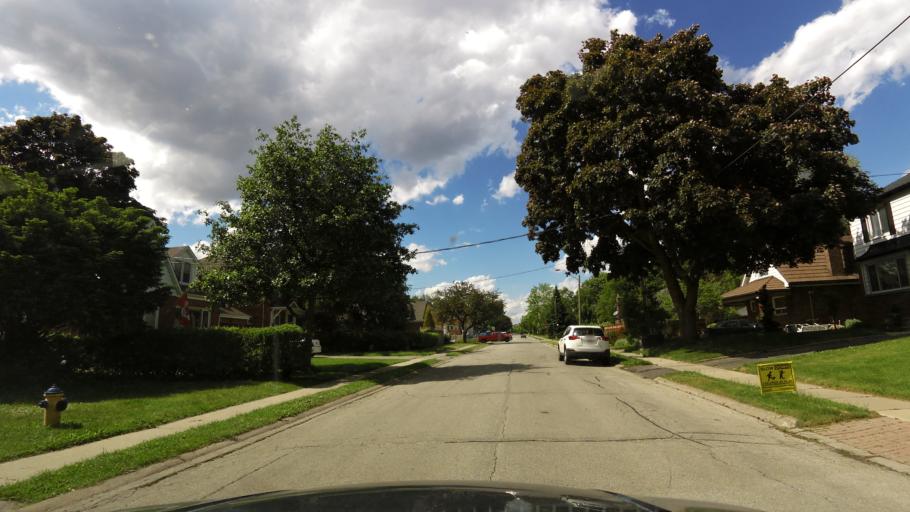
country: CA
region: Ontario
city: Etobicoke
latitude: 43.5904
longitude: -79.5368
